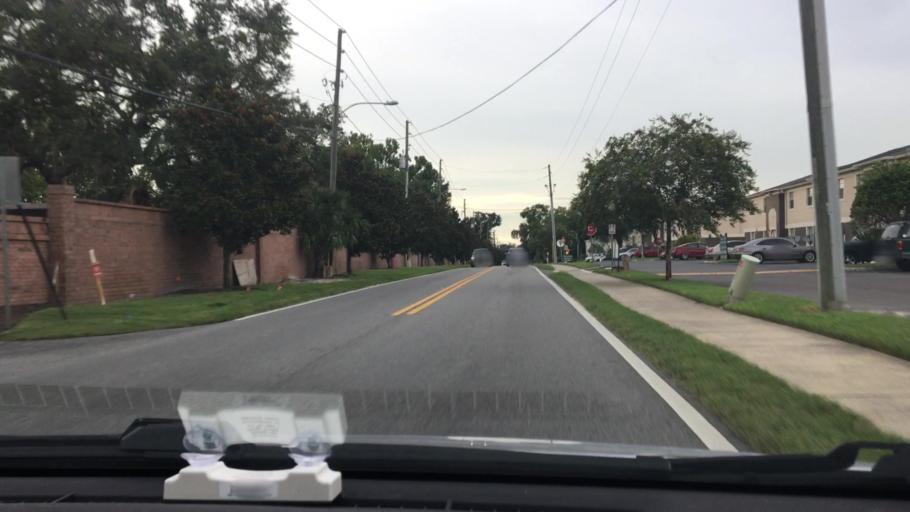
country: US
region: Florida
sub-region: Seminole County
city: Altamonte Springs
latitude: 28.6451
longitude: -81.3904
